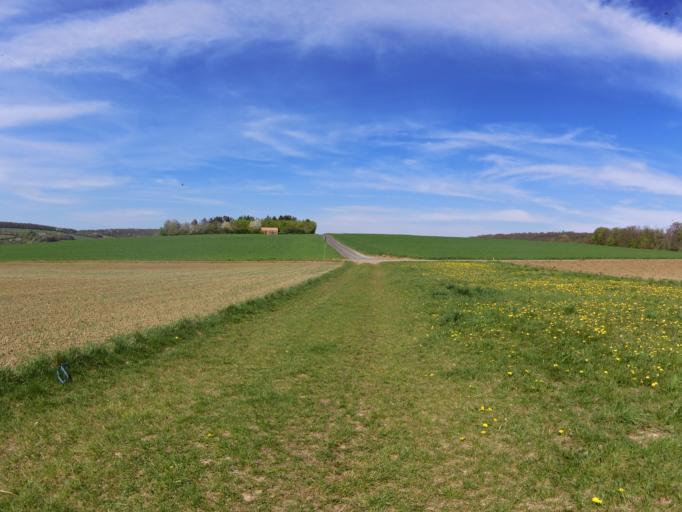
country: DE
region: Bavaria
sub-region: Regierungsbezirk Unterfranken
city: Rimpar
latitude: 49.8580
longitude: 9.9754
